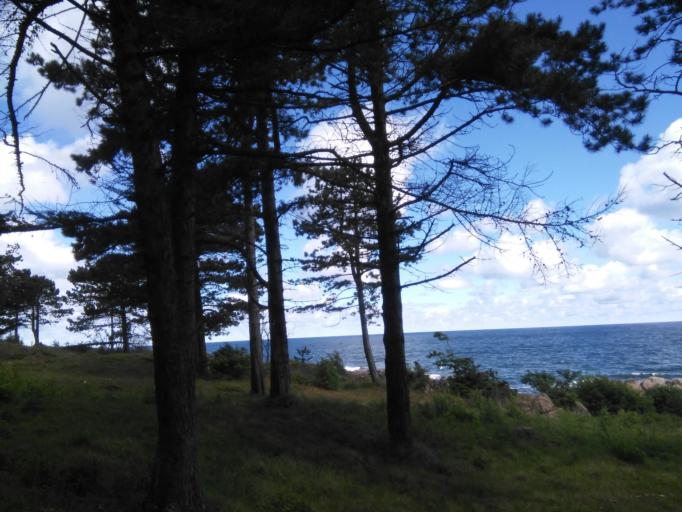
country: DK
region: Capital Region
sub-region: Bornholm Kommune
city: Ronne
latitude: 55.2969
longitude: 14.7755
